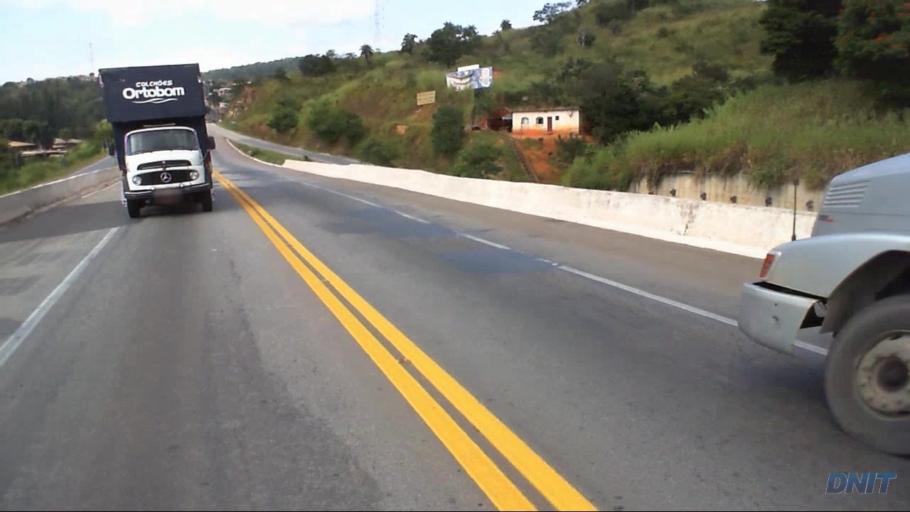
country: BR
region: Minas Gerais
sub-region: Santa Luzia
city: Santa Luzia
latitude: -19.8345
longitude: -43.8552
